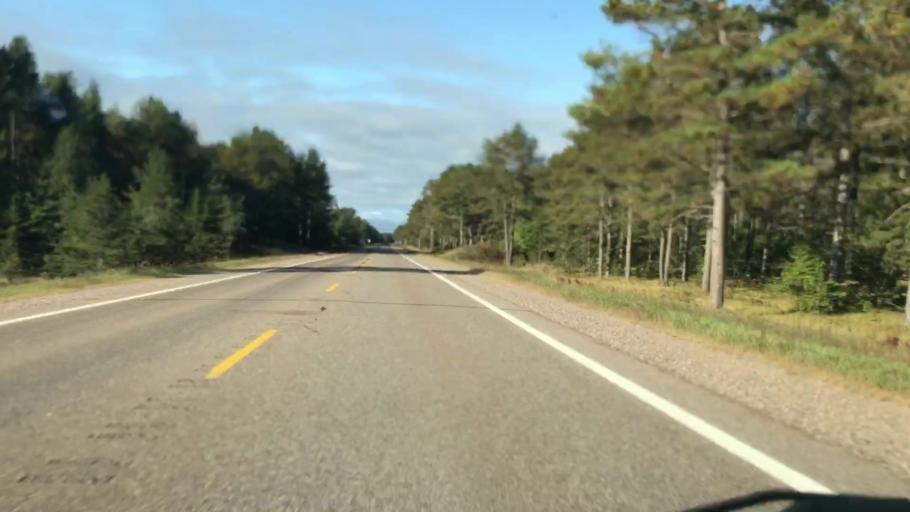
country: US
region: Michigan
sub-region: Mackinac County
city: Saint Ignace
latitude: 46.3545
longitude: -84.8986
